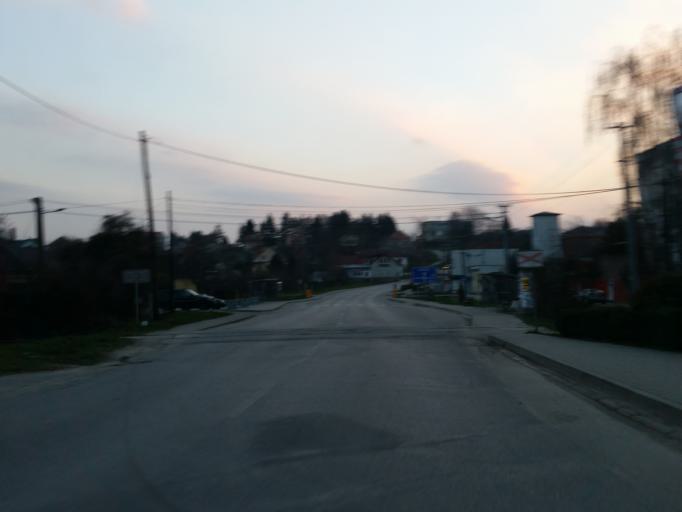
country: SK
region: Trnavsky
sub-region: Okres Trnava
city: Piestany
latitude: 48.5477
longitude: 17.9406
